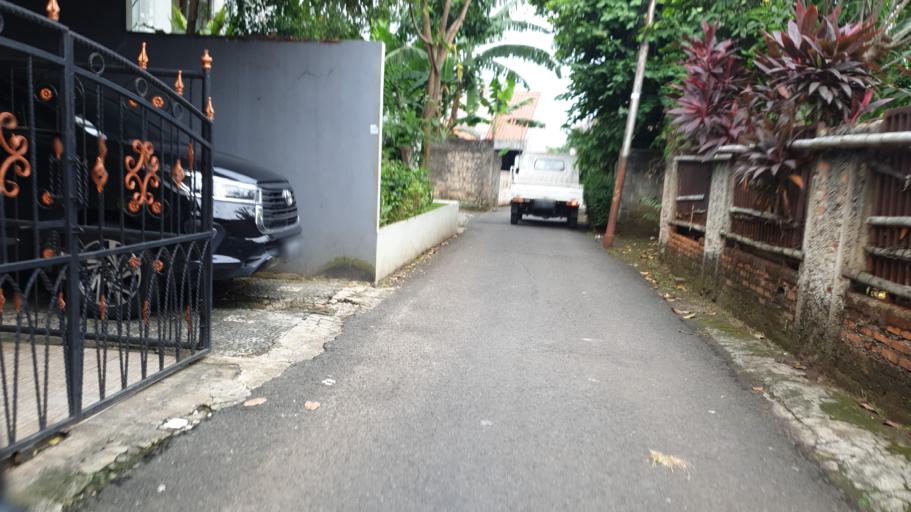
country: ID
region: West Java
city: Depok
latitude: -6.3342
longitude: 106.8210
